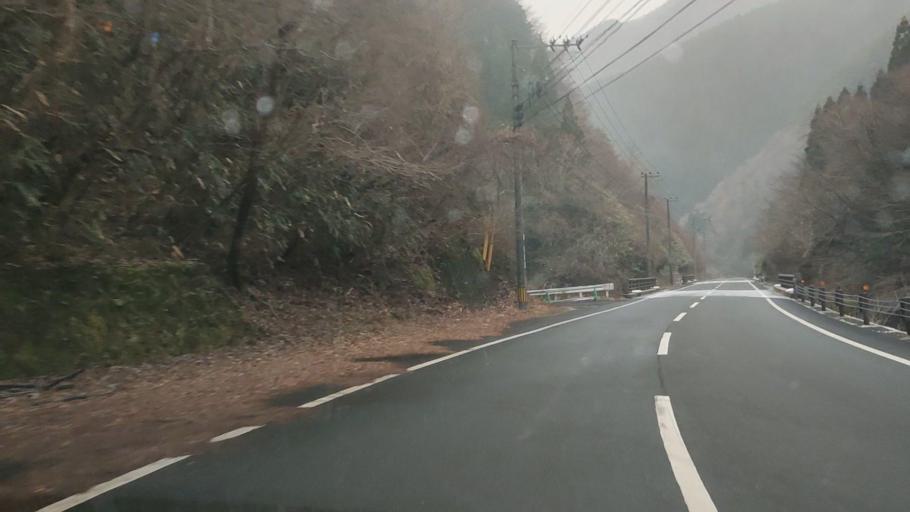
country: JP
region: Kumamoto
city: Matsubase
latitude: 32.5532
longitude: 130.9342
